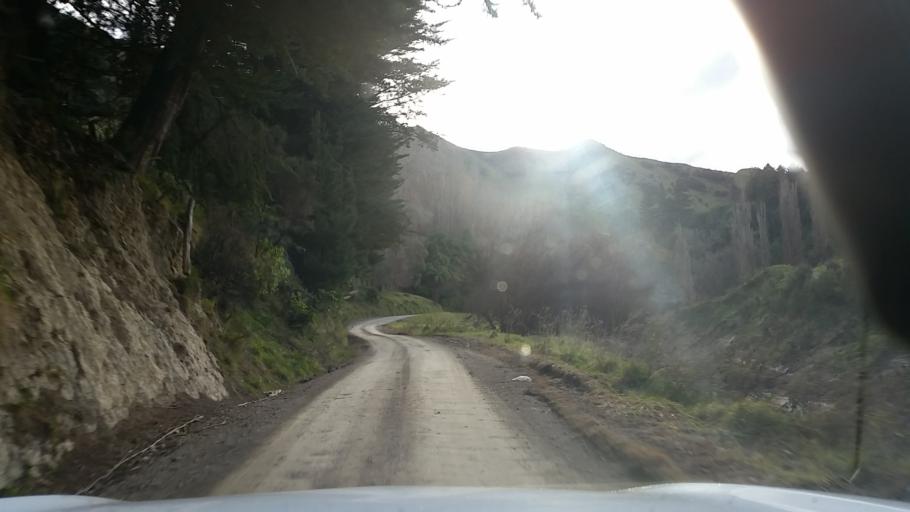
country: NZ
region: Taranaki
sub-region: South Taranaki District
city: Patea
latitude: -39.5650
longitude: 174.8062
